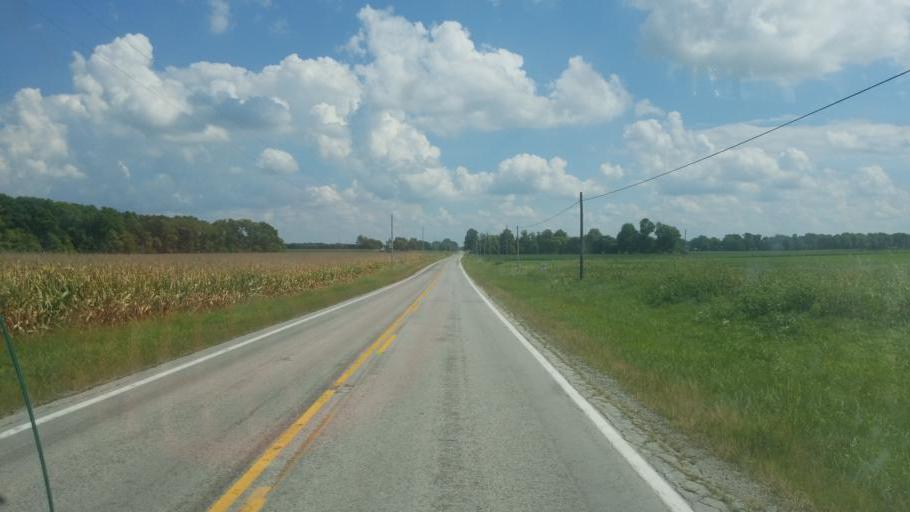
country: US
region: Ohio
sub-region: Hancock County
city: Arlington
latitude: 40.8924
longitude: -83.7105
